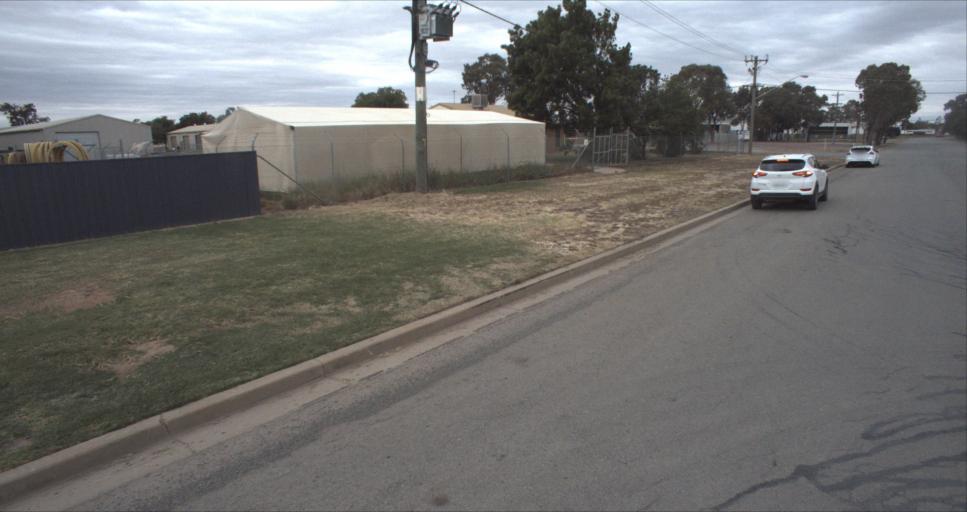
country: AU
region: New South Wales
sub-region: Leeton
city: Leeton
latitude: -34.5480
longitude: 146.3908
